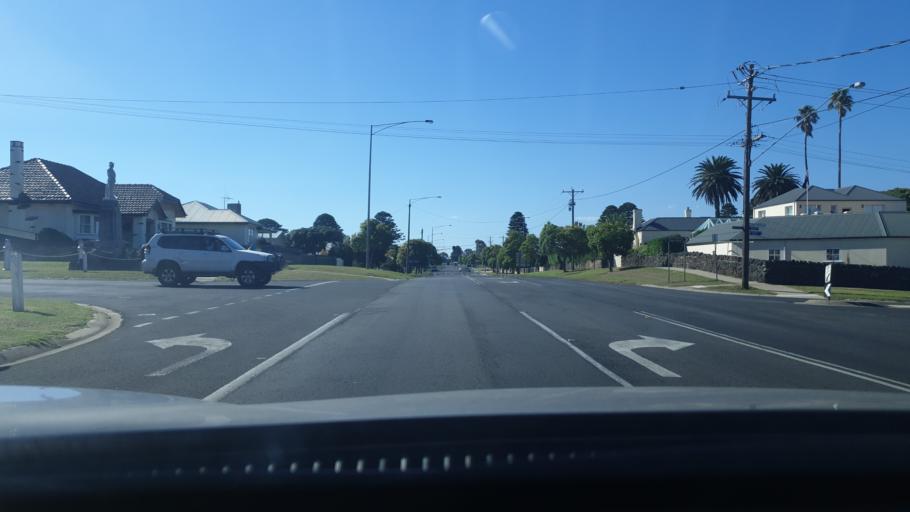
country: AU
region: Victoria
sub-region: Moyne
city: Port Fairy
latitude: -38.3829
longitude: 142.2290
